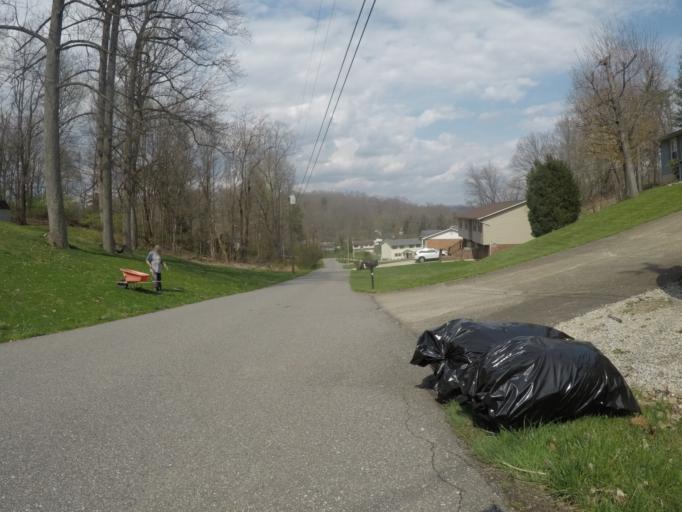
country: US
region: West Virginia
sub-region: Cabell County
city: Pea Ridge
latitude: 38.3997
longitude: -82.3355
